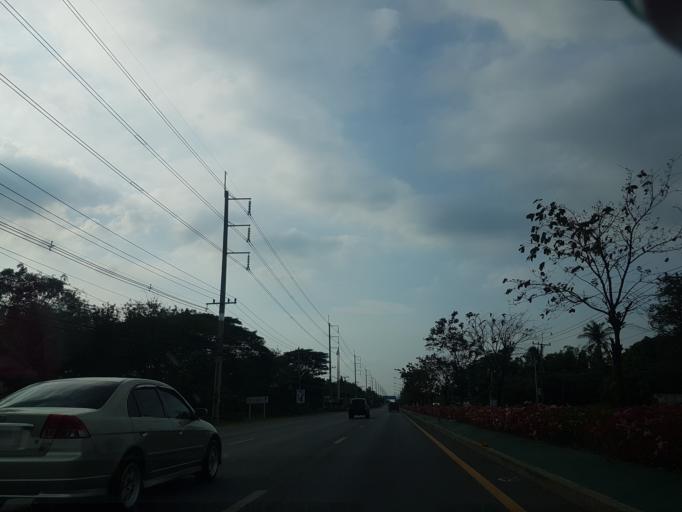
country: TH
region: Sara Buri
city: Phra Phutthabat
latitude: 14.7508
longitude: 100.7440
